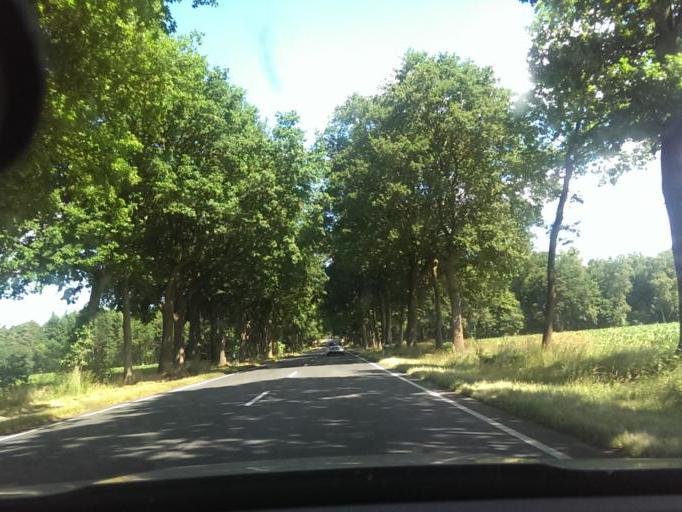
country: DE
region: Lower Saxony
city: Kirchlinteln
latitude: 52.9878
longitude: 9.2640
